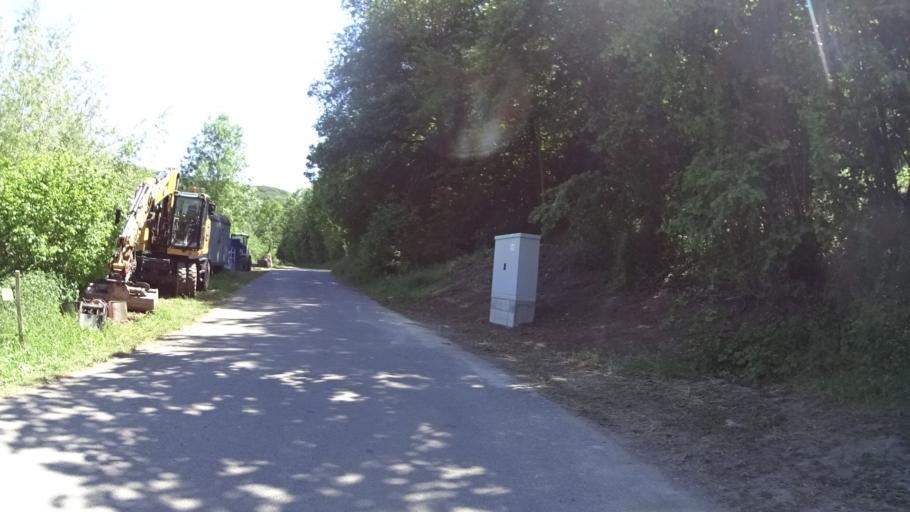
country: DE
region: Bavaria
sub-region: Regierungsbezirk Mittelfranken
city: Adelshofen
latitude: 49.4142
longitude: 10.1499
